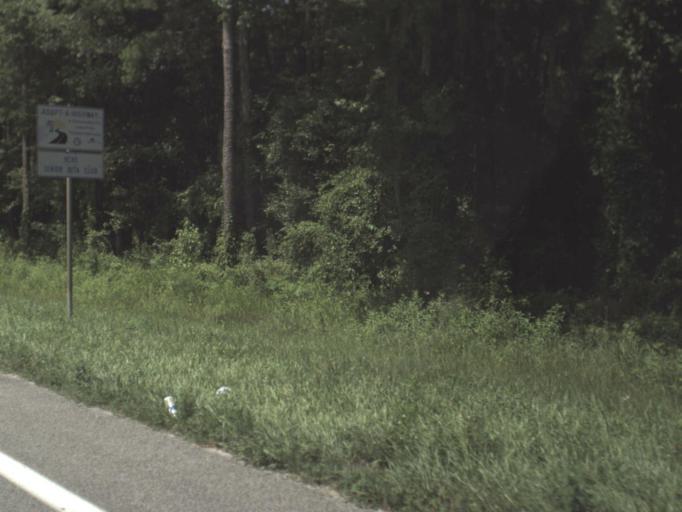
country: US
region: Florida
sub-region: Hamilton County
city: Jasper
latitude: 30.4838
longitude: -82.9301
